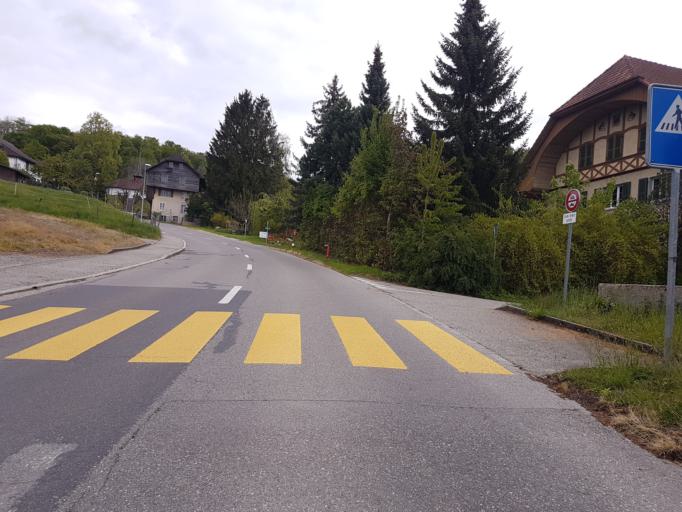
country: CH
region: Bern
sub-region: Seeland District
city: Arch
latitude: 47.1646
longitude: 7.4309
